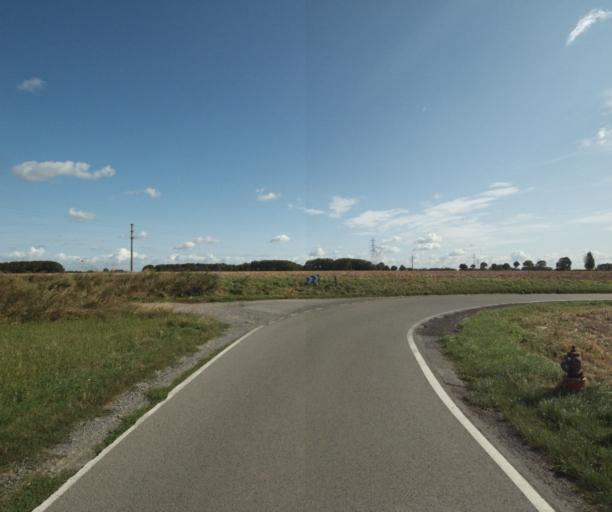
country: FR
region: Nord-Pas-de-Calais
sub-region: Departement du Nord
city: Sainghin-en-Melantois
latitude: 50.5951
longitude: 3.1595
